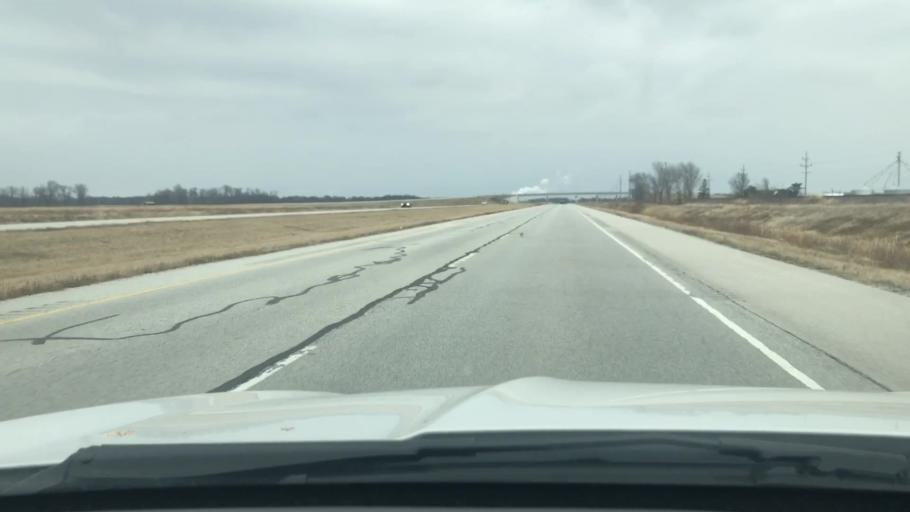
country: US
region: Indiana
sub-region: Cass County
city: Georgetown
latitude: 40.6881
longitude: -86.4863
